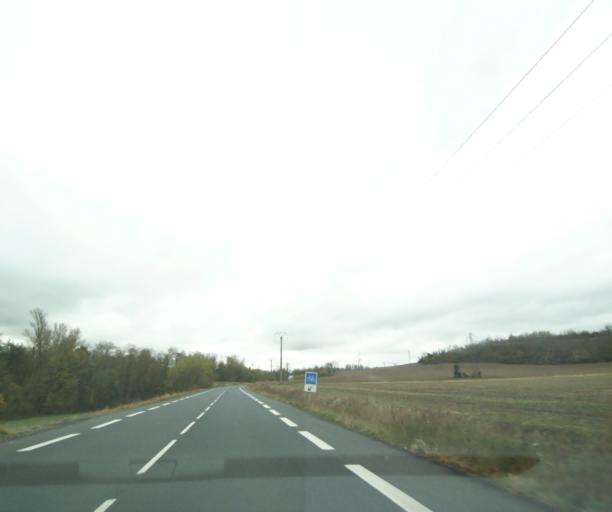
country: FR
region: Auvergne
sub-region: Departement du Puy-de-Dome
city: Dallet
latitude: 45.7793
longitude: 3.2365
